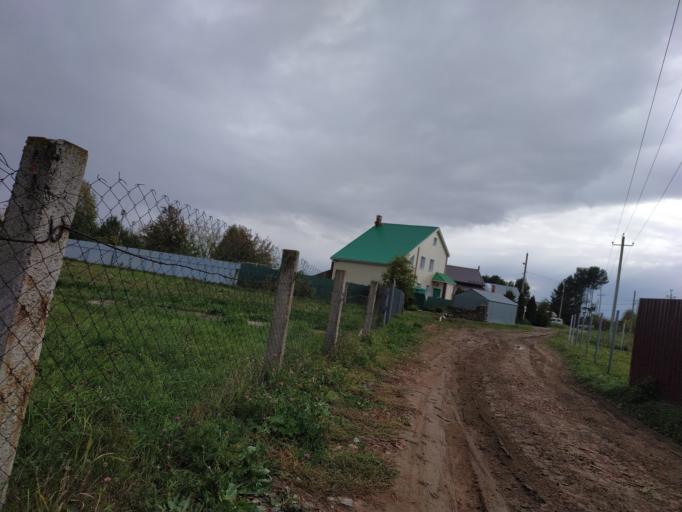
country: RU
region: Chuvashia
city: Ishley
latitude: 56.1293
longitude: 47.0912
